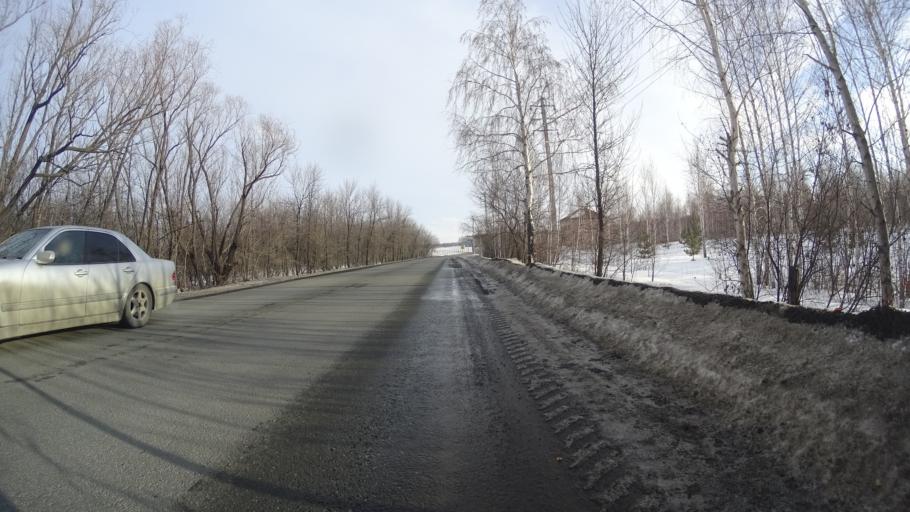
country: RU
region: Chelyabinsk
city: Sargazy
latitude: 55.1358
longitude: 61.2840
